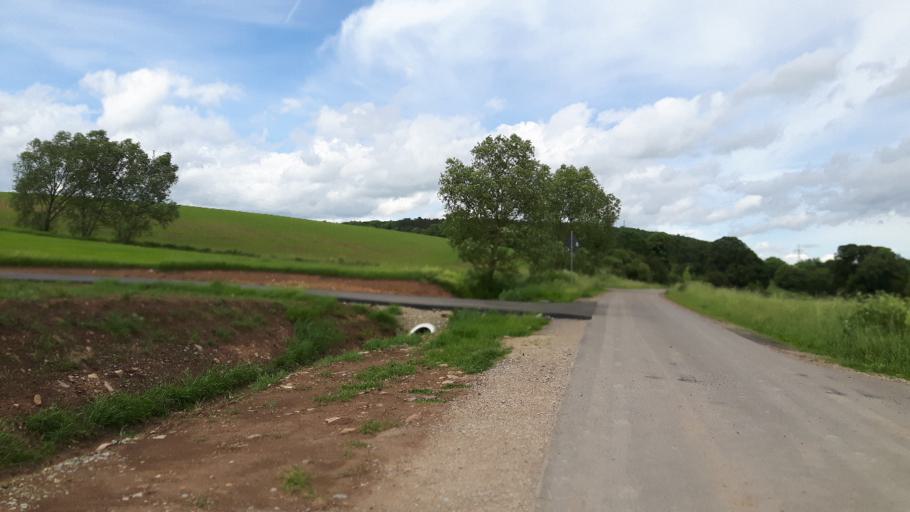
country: DE
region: Thuringia
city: Behringen
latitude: 50.7614
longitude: 11.0482
